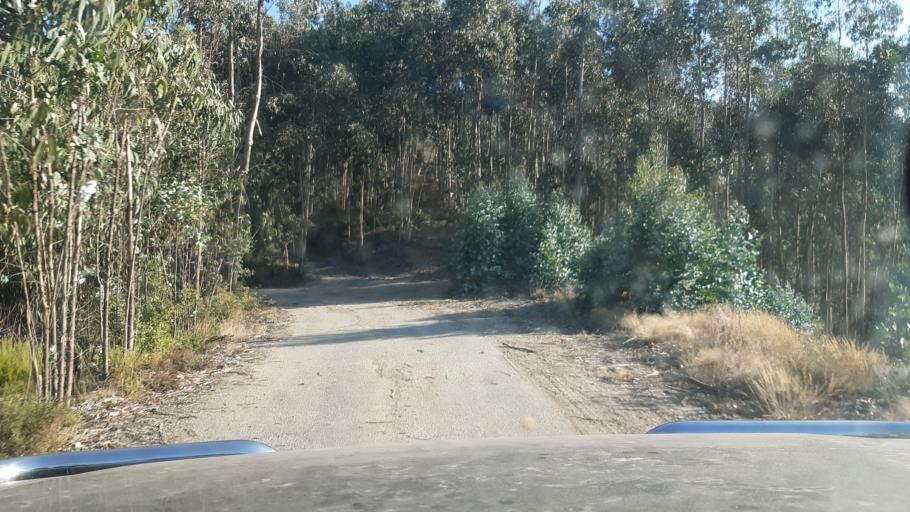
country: PT
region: Viseu
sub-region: Mortagua
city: Mortagua
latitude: 40.5242
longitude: -8.2537
